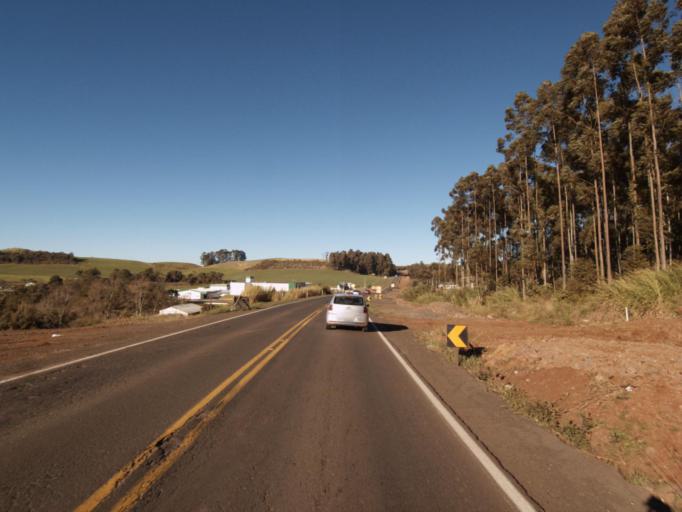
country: AR
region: Misiones
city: Bernardo de Irigoyen
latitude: -26.6268
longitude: -53.5160
